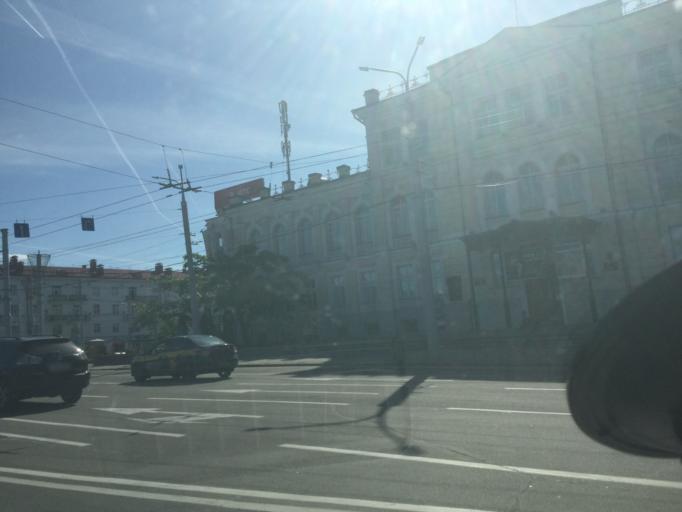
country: BY
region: Vitebsk
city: Vitebsk
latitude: 55.1934
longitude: 30.2065
